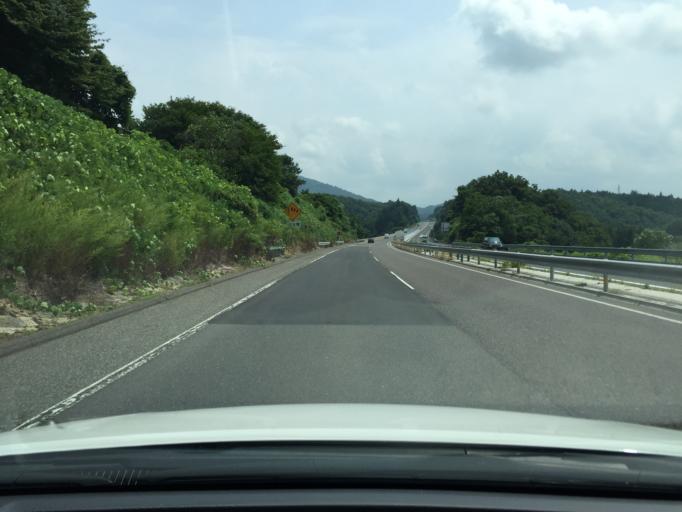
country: JP
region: Fukushima
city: Funehikimachi-funehiki
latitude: 37.4363
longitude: 140.5323
